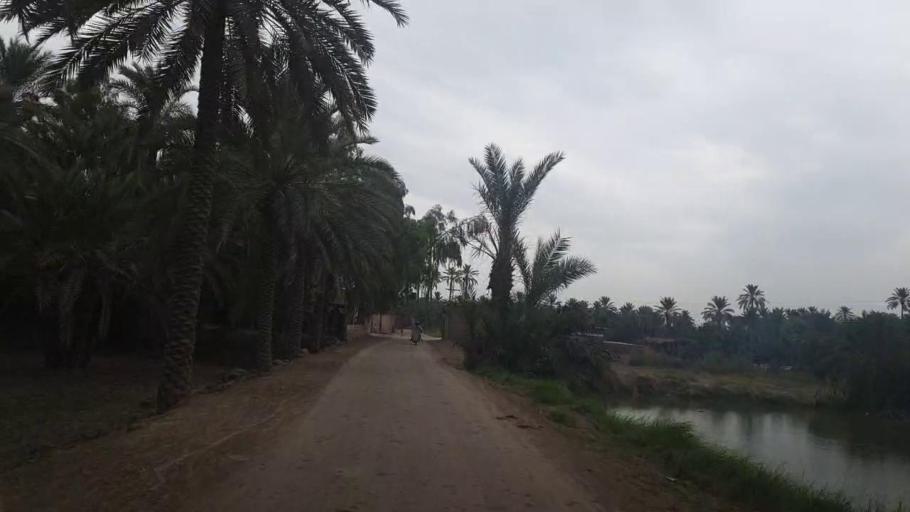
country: PK
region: Sindh
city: Khairpur
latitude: 27.5750
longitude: 68.7450
